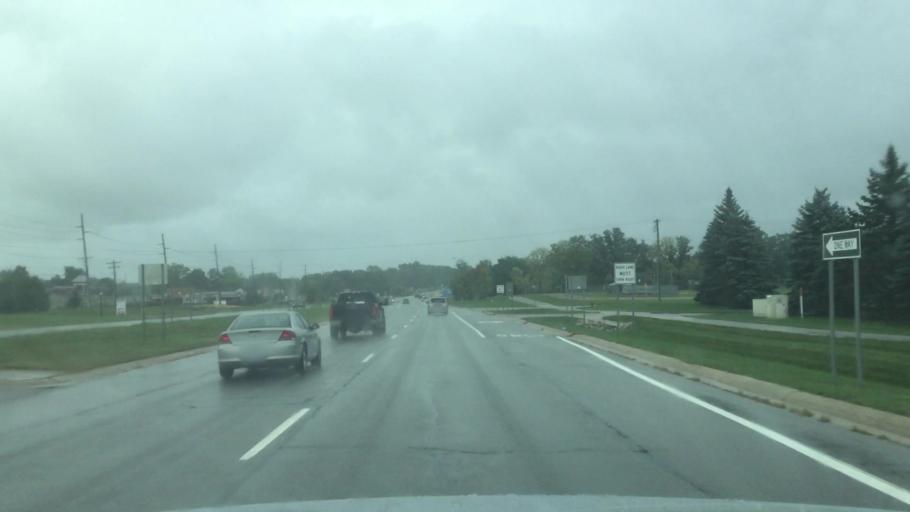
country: US
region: Michigan
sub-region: Livingston County
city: Howell
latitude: 42.6220
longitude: -83.9336
